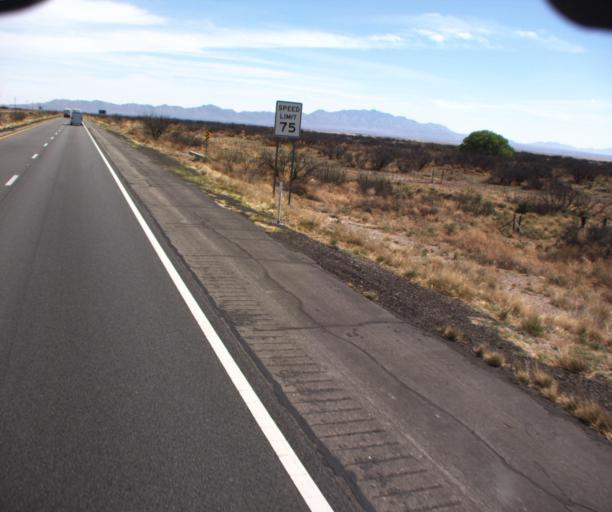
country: US
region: Arizona
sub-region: Cochise County
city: Willcox
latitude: 32.1825
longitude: -109.9389
